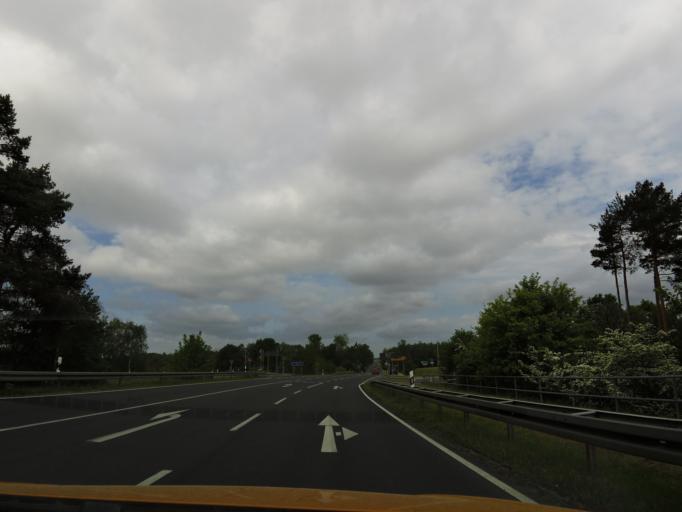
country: DE
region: Brandenburg
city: Niemegk
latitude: 52.0970
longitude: 12.6899
